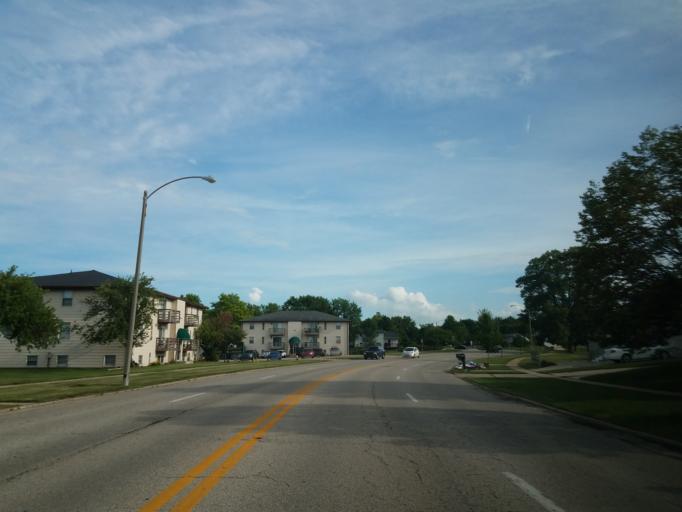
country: US
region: Illinois
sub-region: McLean County
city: Normal
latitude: 40.4950
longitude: -88.9428
